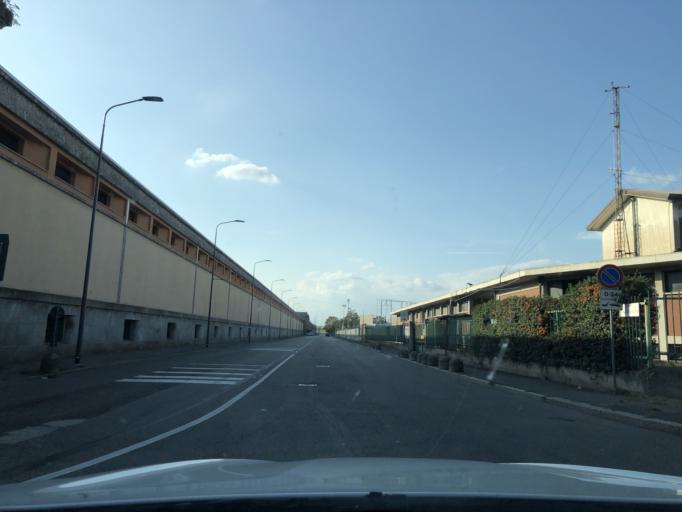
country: IT
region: Lombardy
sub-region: Citta metropolitana di Milano
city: Baranzate
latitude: 45.5067
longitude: 9.1228
